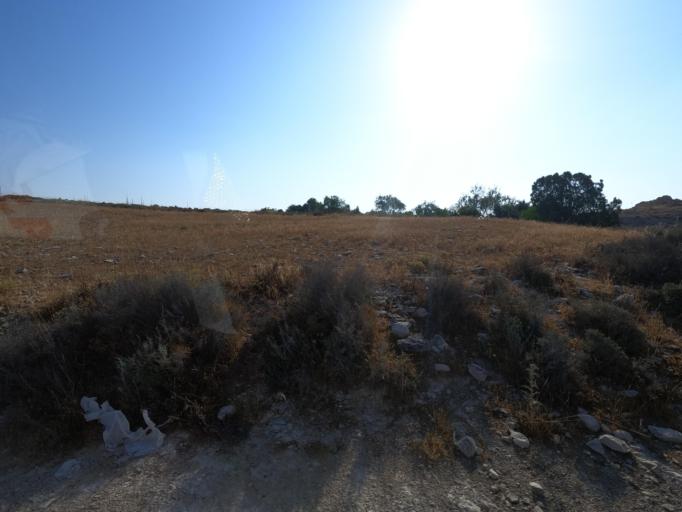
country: CY
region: Lefkosia
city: Lympia
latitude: 34.9911
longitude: 33.4502
